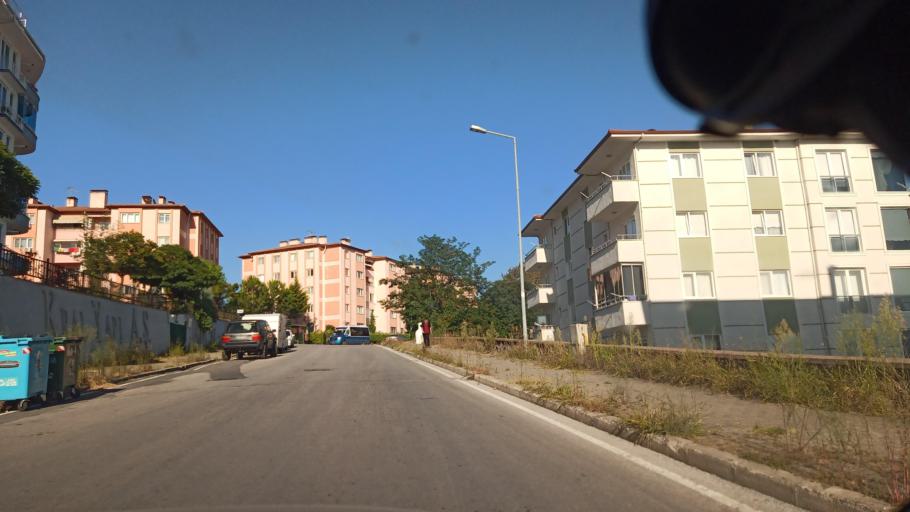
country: TR
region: Sakarya
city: Kazimpasa
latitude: 40.8553
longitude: 30.2916
